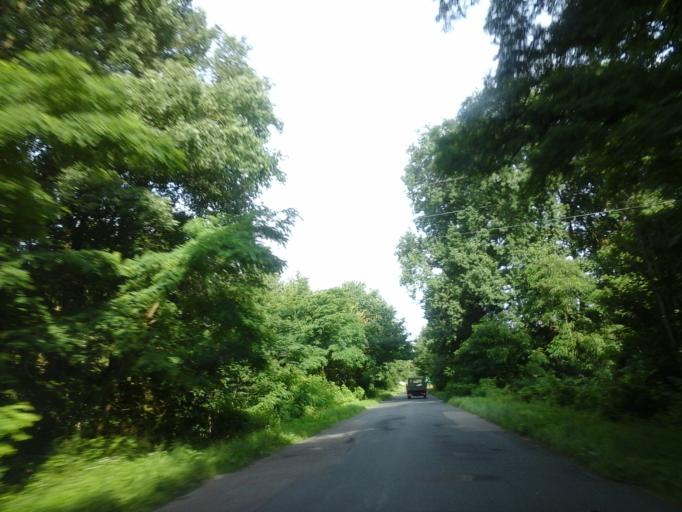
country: PL
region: West Pomeranian Voivodeship
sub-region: Powiat stargardzki
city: Dolice
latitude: 53.2399
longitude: 15.2425
